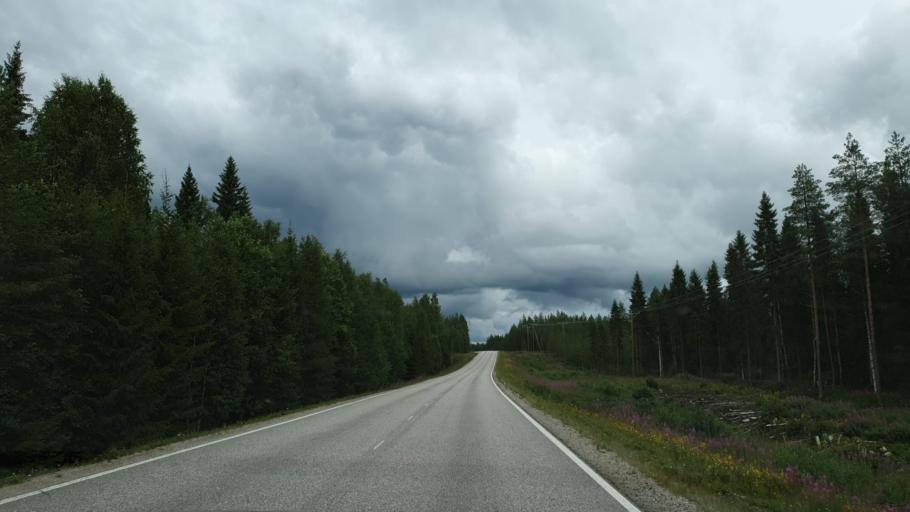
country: FI
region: Kainuu
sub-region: Kehys-Kainuu
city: Kuhmo
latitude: 64.3267
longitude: 29.8728
